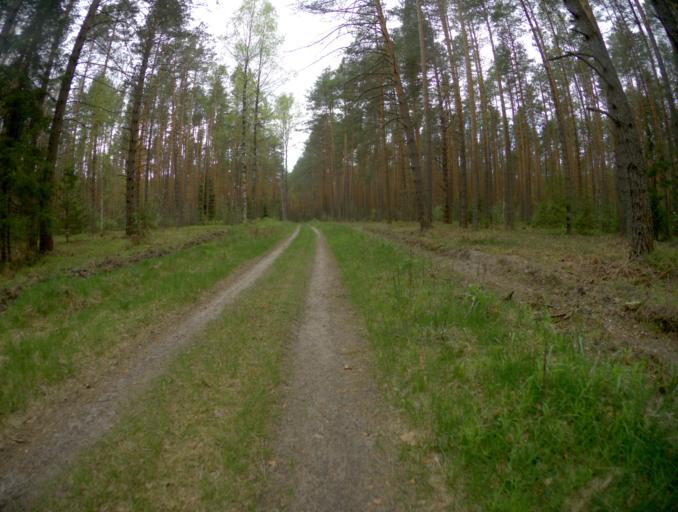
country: RU
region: Vladimir
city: Golovino
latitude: 55.9159
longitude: 40.4024
